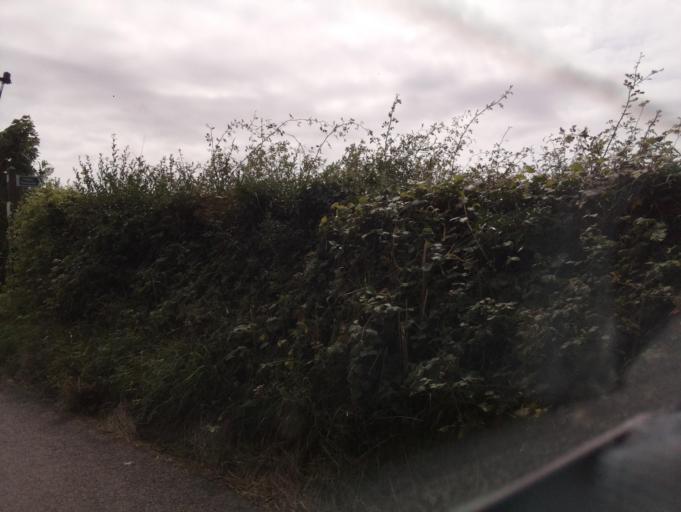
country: GB
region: England
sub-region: Borough of Torbay
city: Paignton
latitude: 50.3973
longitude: -3.5756
